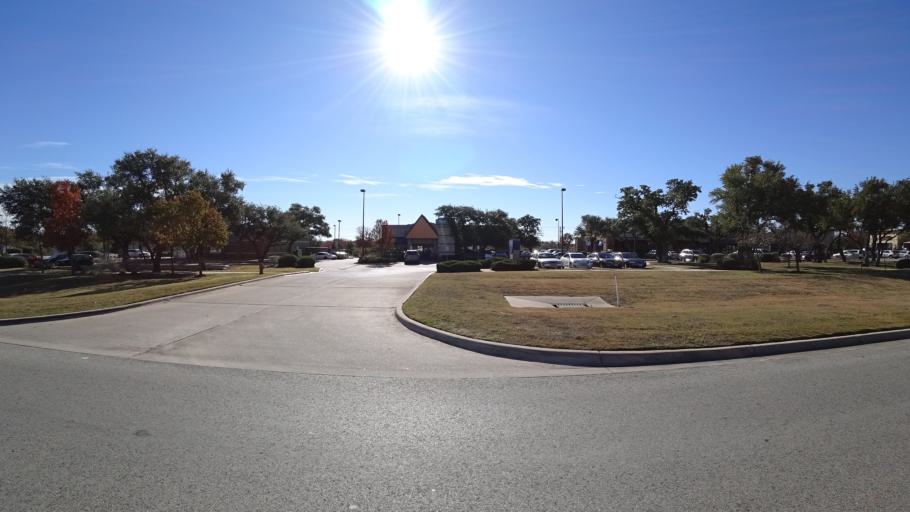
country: US
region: Texas
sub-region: Williamson County
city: Cedar Park
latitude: 30.5235
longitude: -97.8216
